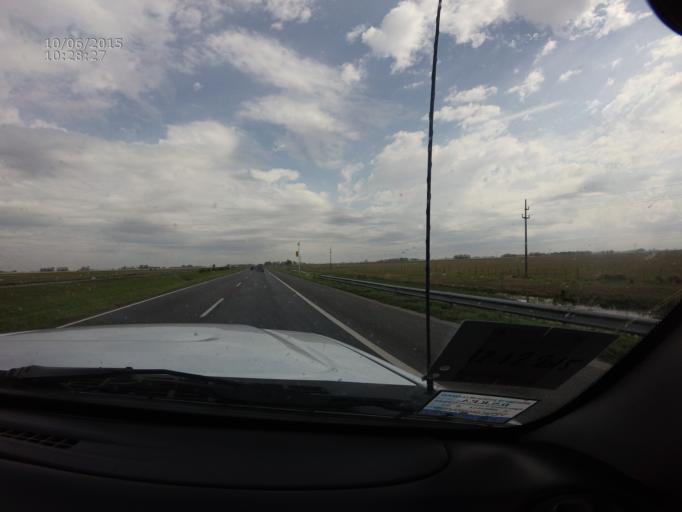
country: AR
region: Buenos Aires
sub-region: Partido de Ramallo
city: Ramallo
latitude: -33.6559
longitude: -59.9618
